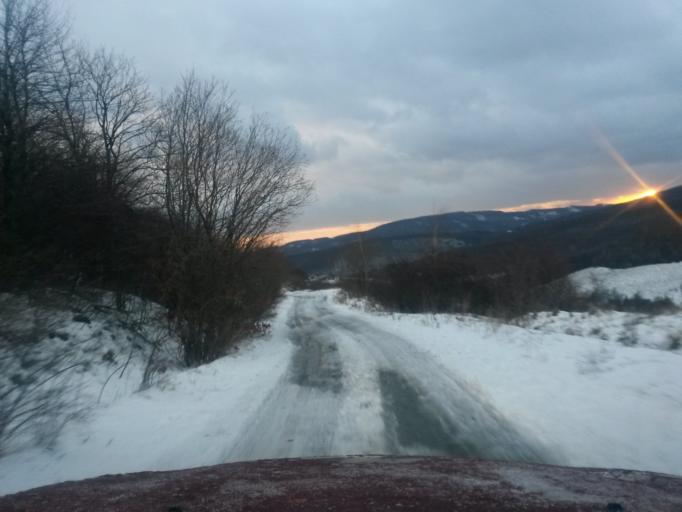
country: SK
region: Kosicky
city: Kosice
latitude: 48.7524
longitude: 21.1240
